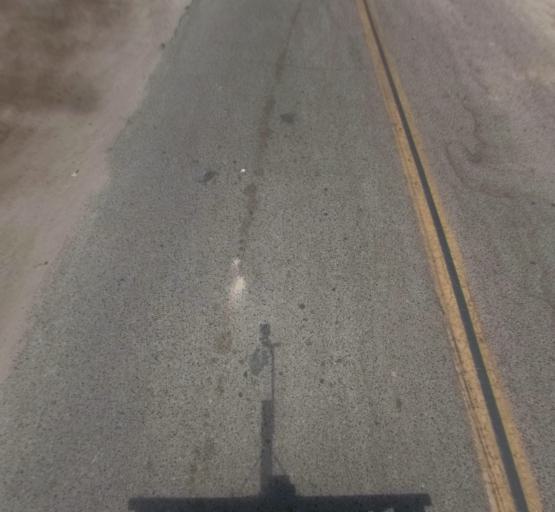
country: US
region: California
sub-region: Fresno County
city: Kerman
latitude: 36.8364
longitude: -120.2114
